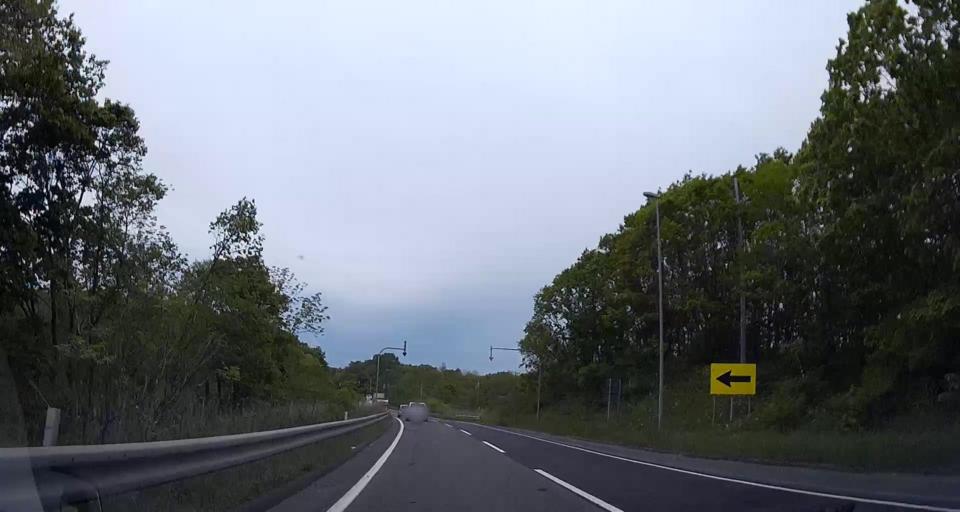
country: JP
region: Hokkaido
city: Chitose
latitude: 42.7083
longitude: 141.7452
